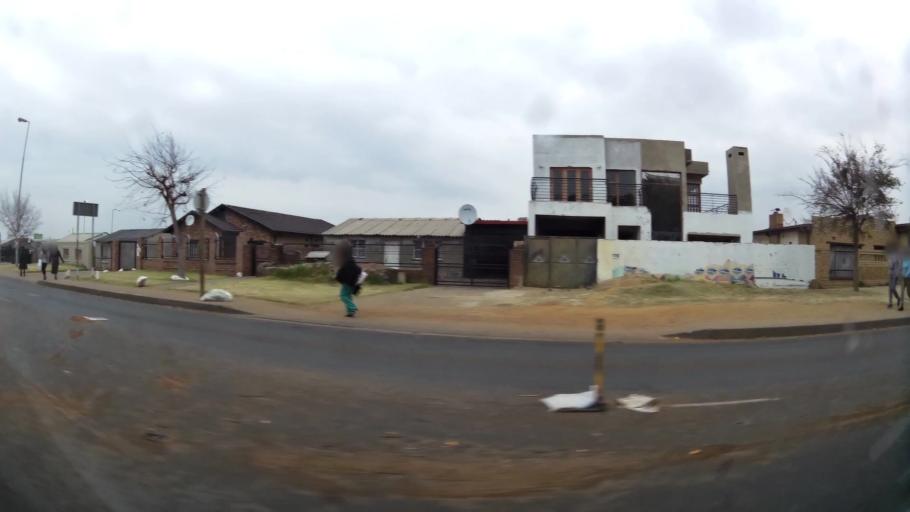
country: ZA
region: Gauteng
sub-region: City of Johannesburg Metropolitan Municipality
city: Soweto
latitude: -26.2515
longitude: 27.8541
